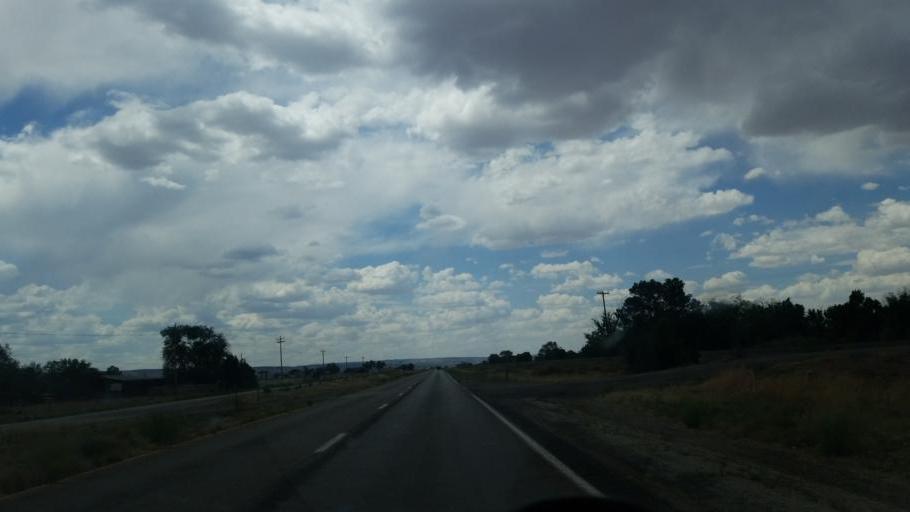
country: US
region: New Mexico
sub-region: Cibola County
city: Milan
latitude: 35.2318
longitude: -107.9309
